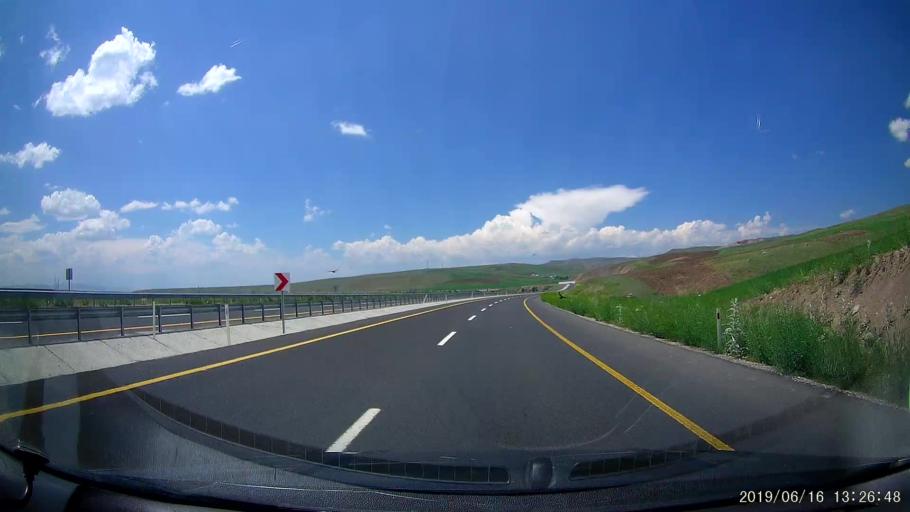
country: TR
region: Agri
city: Taslicay
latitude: 39.6623
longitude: 43.3198
